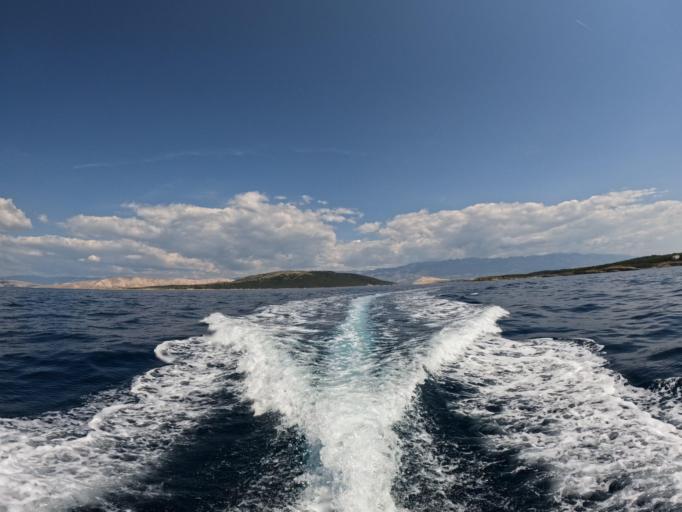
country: HR
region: Primorsko-Goranska
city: Lopar
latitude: 44.8566
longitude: 14.7152
